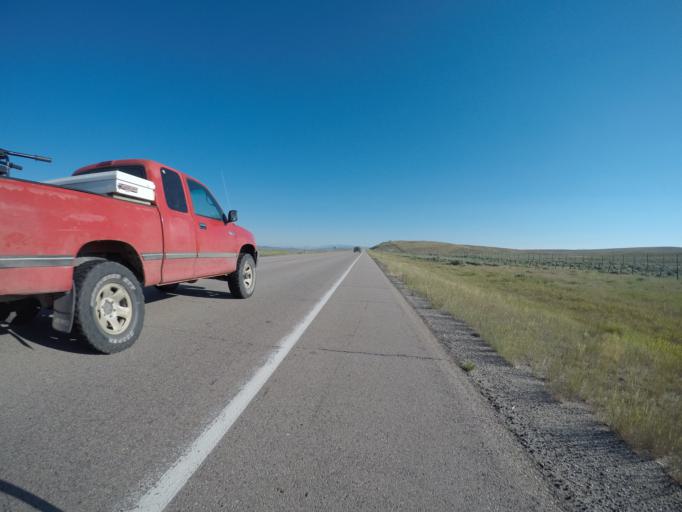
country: US
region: Wyoming
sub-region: Sublette County
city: Pinedale
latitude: 42.9389
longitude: -110.0823
